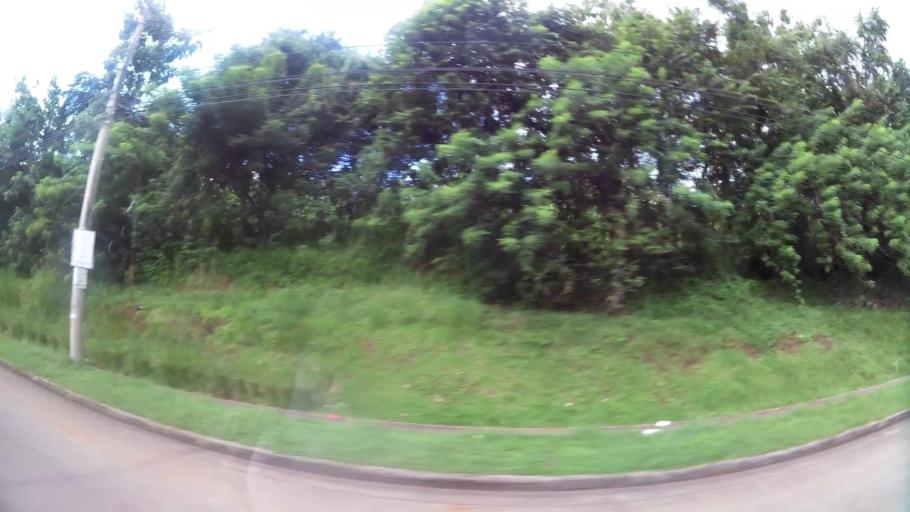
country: PA
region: Panama
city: Nuevo Arraijan
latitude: 8.9281
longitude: -79.7374
